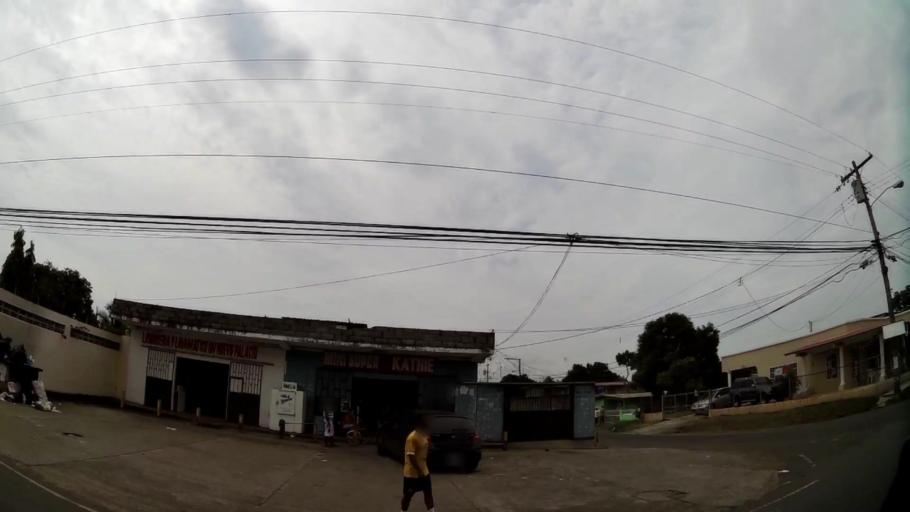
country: PA
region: Panama
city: San Miguelito
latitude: 9.0485
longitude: -79.4364
